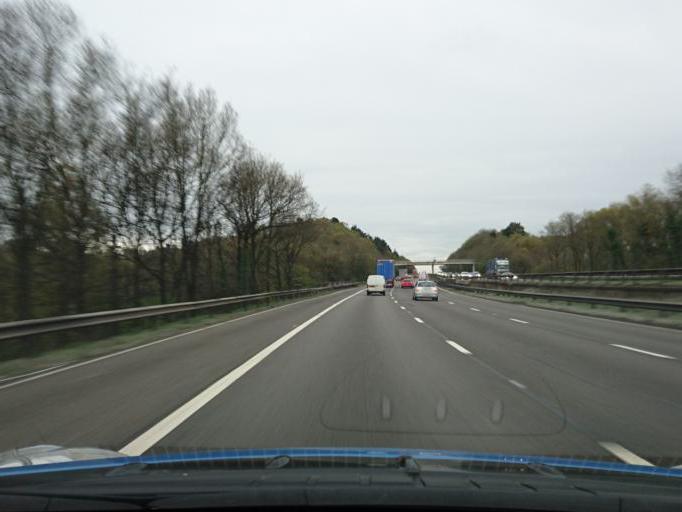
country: GB
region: England
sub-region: Staffordshire
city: Newcastle under Lyme
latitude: 52.9671
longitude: -2.2215
